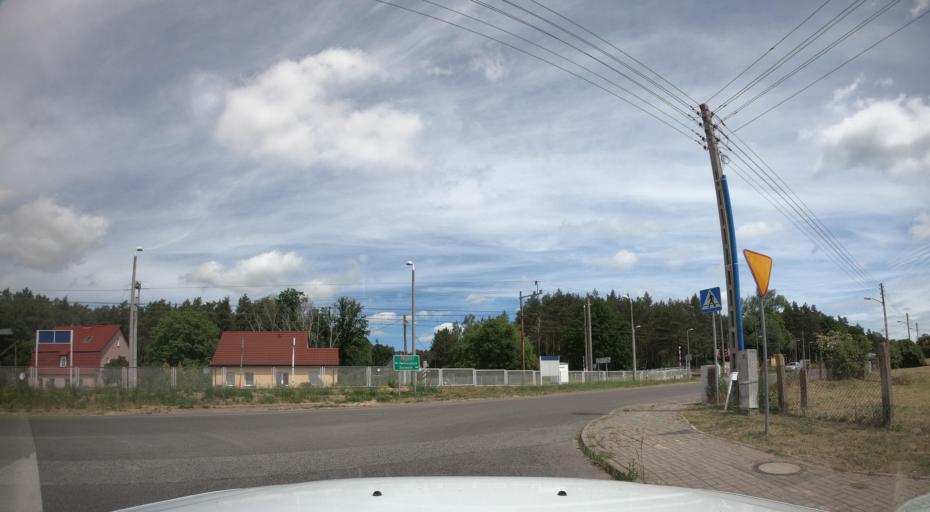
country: PL
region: West Pomeranian Voivodeship
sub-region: Powiat kamienski
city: Wolin
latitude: 53.8438
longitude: 14.7169
